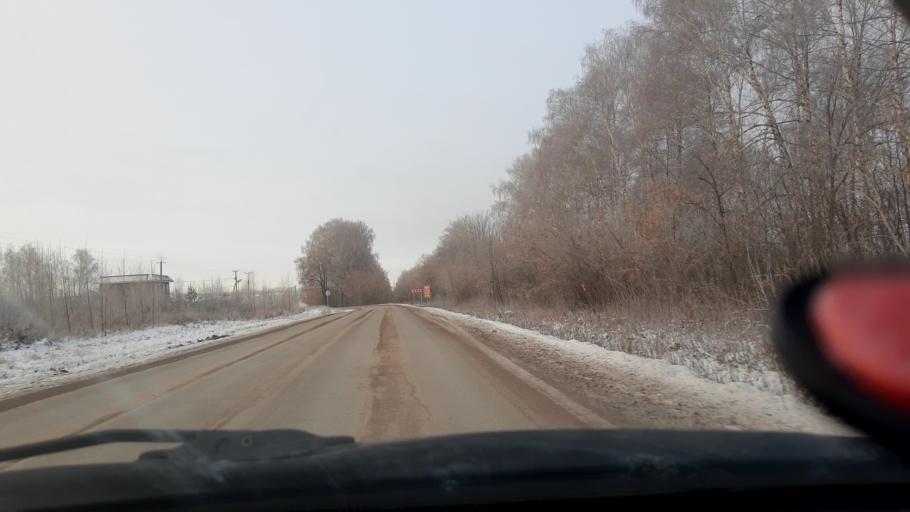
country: RU
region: Bashkortostan
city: Iglino
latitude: 54.8352
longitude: 56.4424
